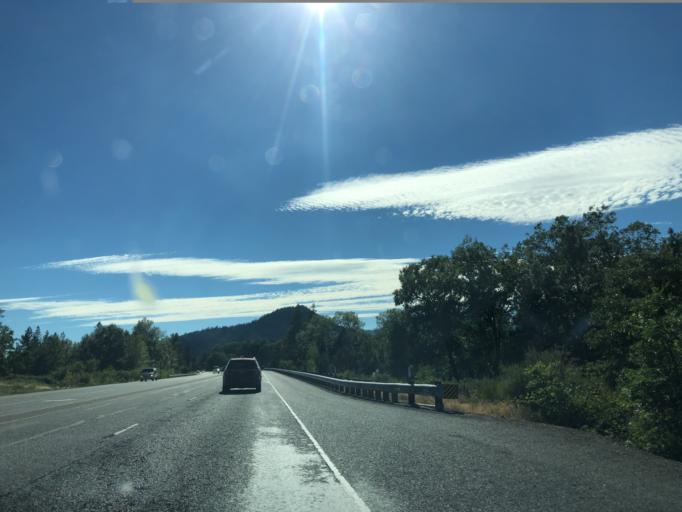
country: US
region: Oregon
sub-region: Josephine County
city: Redwood
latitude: 42.4107
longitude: -123.4269
